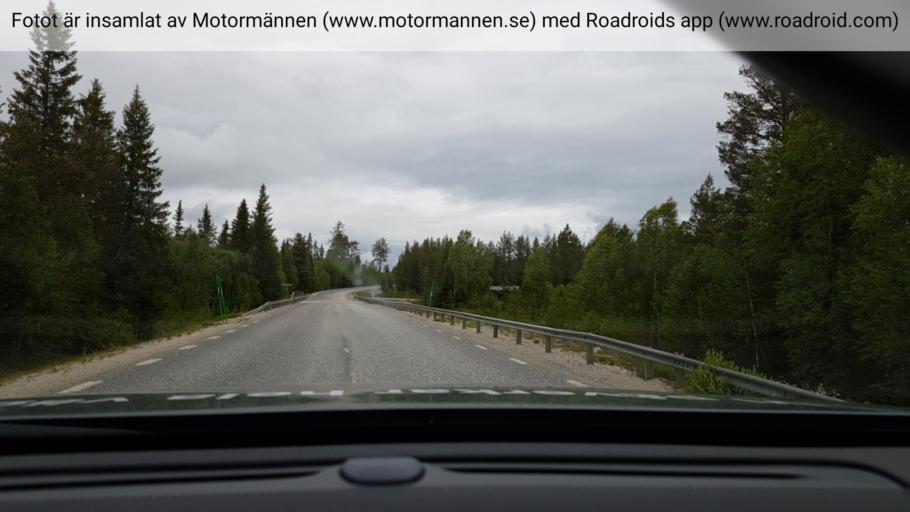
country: SE
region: Vaesterbotten
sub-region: Asele Kommun
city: Insjon
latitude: 64.3515
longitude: 17.8990
